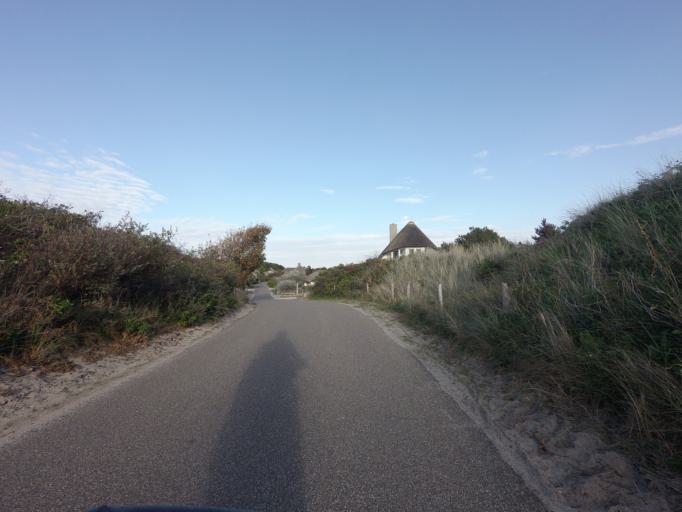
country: NL
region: Friesland
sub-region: Gemeente Ameland
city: Nes
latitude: 53.4579
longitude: 5.7996
